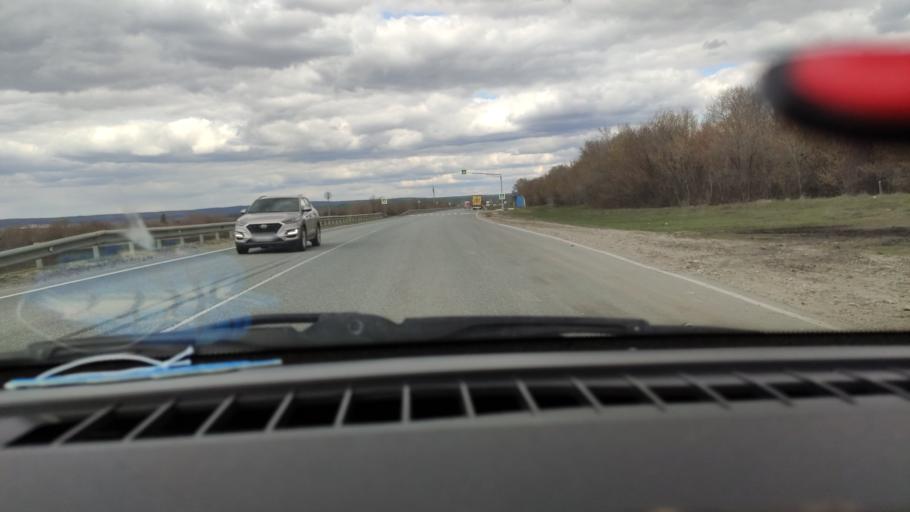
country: RU
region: Saratov
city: Tersa
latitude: 52.0876
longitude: 47.5493
